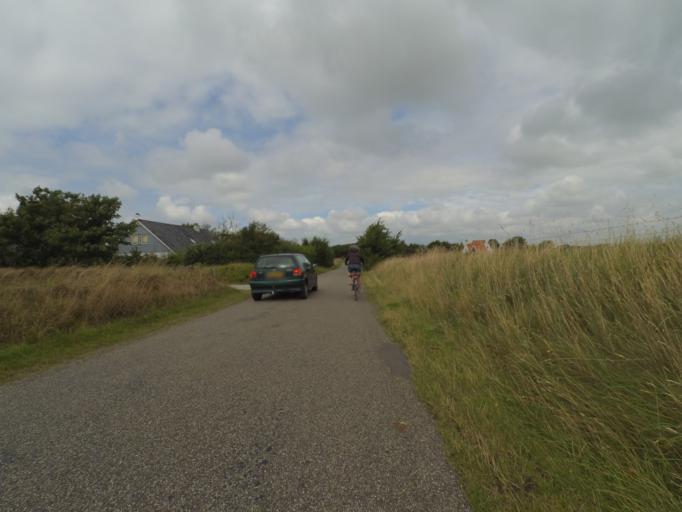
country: NL
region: North Holland
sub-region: Gemeente Texel
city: Den Burg
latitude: 53.0446
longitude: 4.8162
